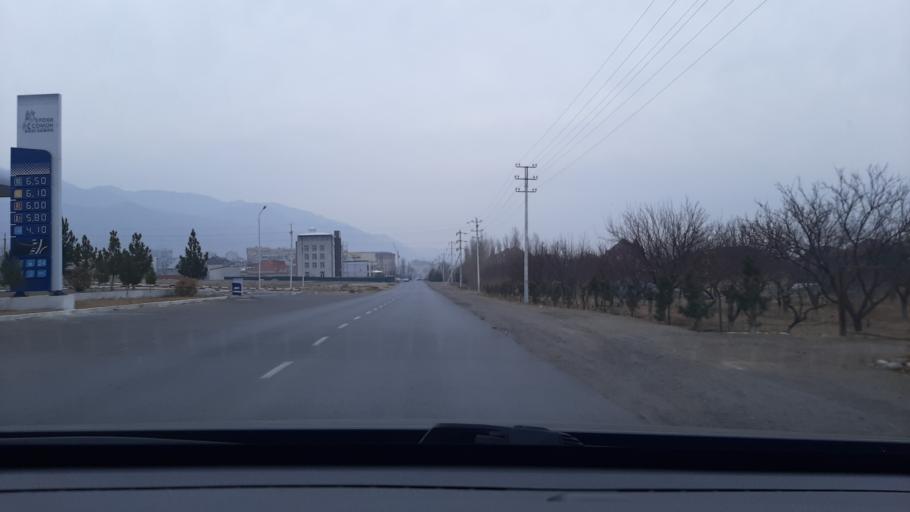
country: TJ
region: Viloyati Sughd
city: Khujand
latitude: 40.2769
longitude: 69.5809
